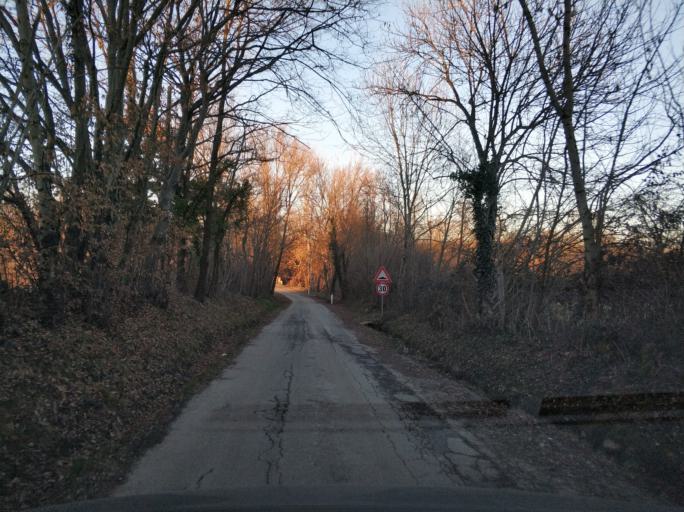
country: IT
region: Piedmont
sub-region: Provincia di Torino
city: San Francesco al Campo
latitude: 45.2438
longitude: 7.6376
